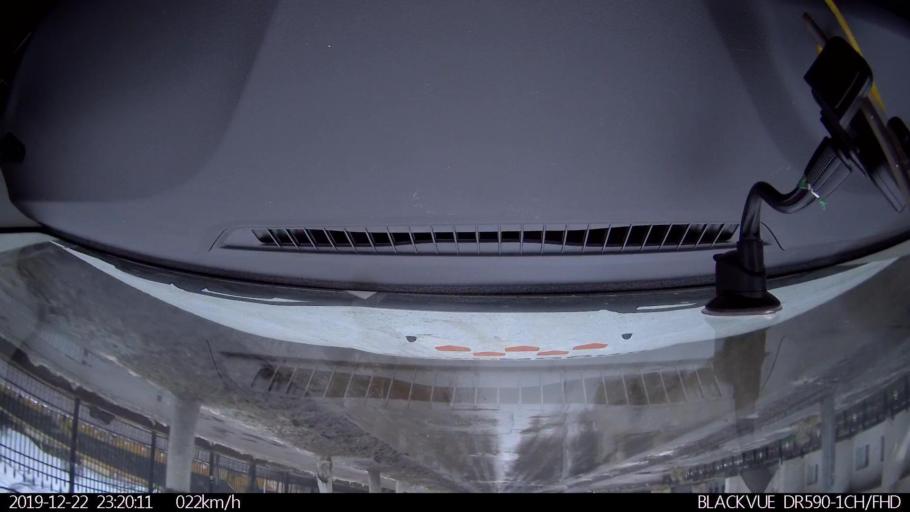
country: RU
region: Nizjnij Novgorod
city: Gorbatovka
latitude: 56.2474
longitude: 43.8611
